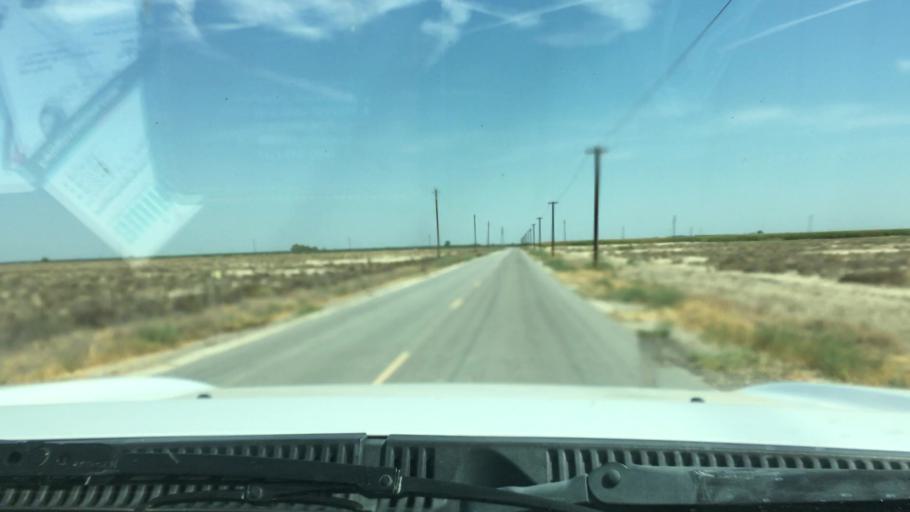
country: US
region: California
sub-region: Kern County
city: Buttonwillow
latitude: 35.4319
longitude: -119.3761
